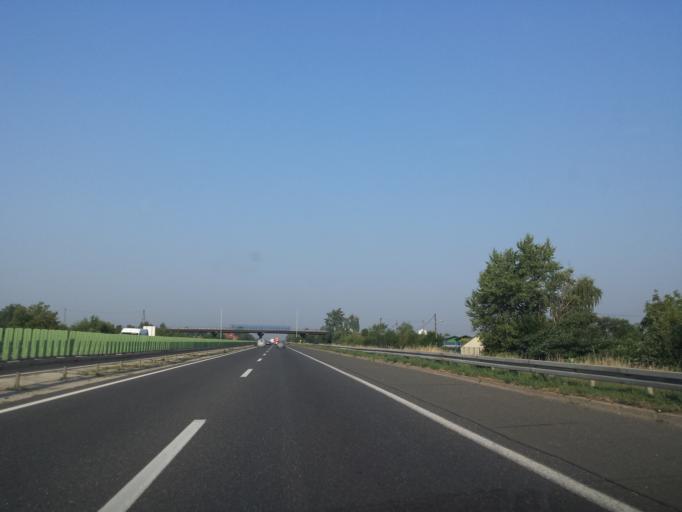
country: HR
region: Grad Zagreb
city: Novi Zagreb
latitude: 45.7527
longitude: 15.9679
